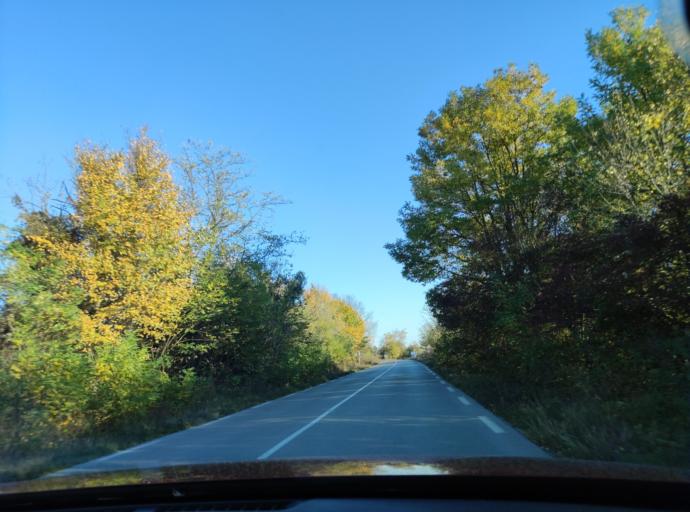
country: BG
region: Montana
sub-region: Obshtina Chiprovtsi
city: Chiprovtsi
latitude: 43.4235
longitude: 23.0142
